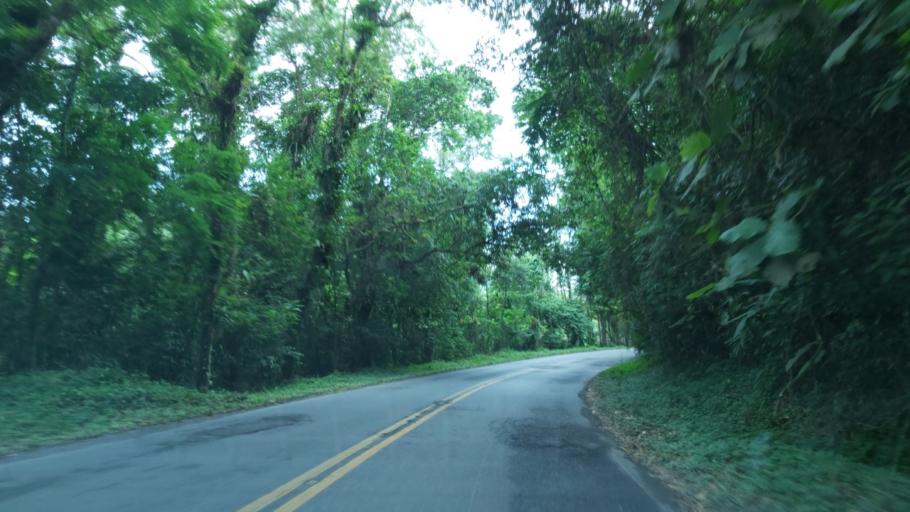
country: BR
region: Sao Paulo
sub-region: Miracatu
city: Miracatu
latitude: -24.0690
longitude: -47.5991
